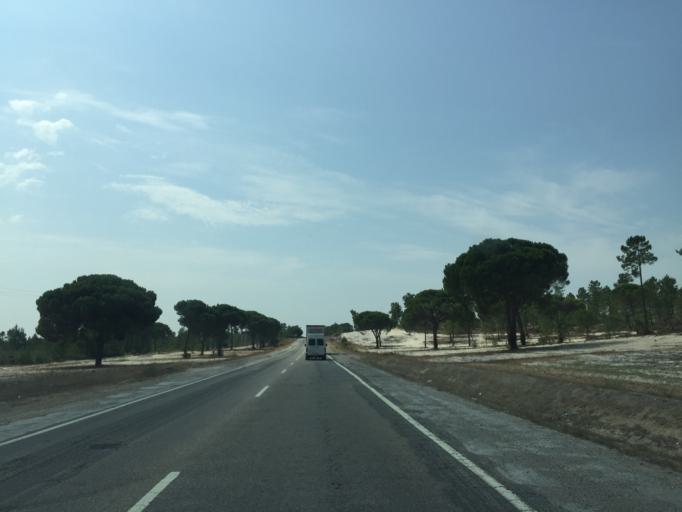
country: PT
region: Setubal
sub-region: Grandola
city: Grandola
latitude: 38.2598
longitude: -8.5451
